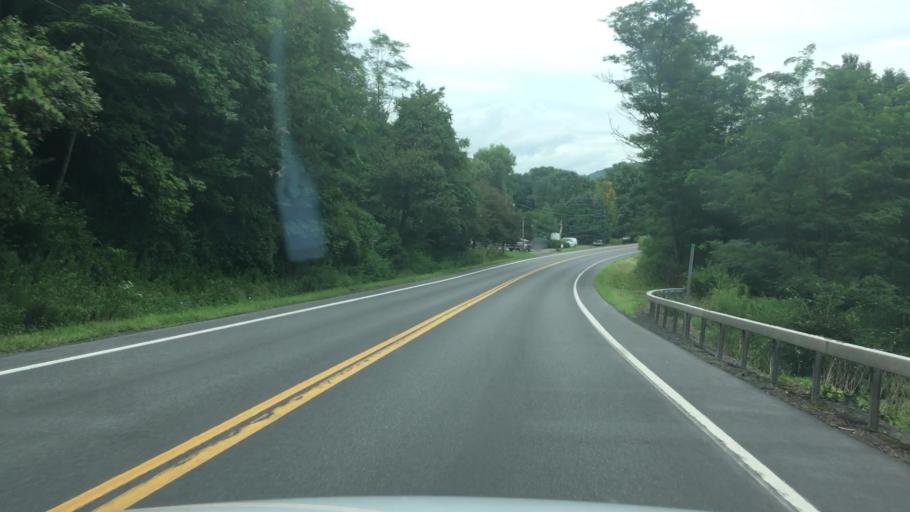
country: US
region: New York
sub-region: Otsego County
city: Otego
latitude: 42.4117
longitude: -75.1496
